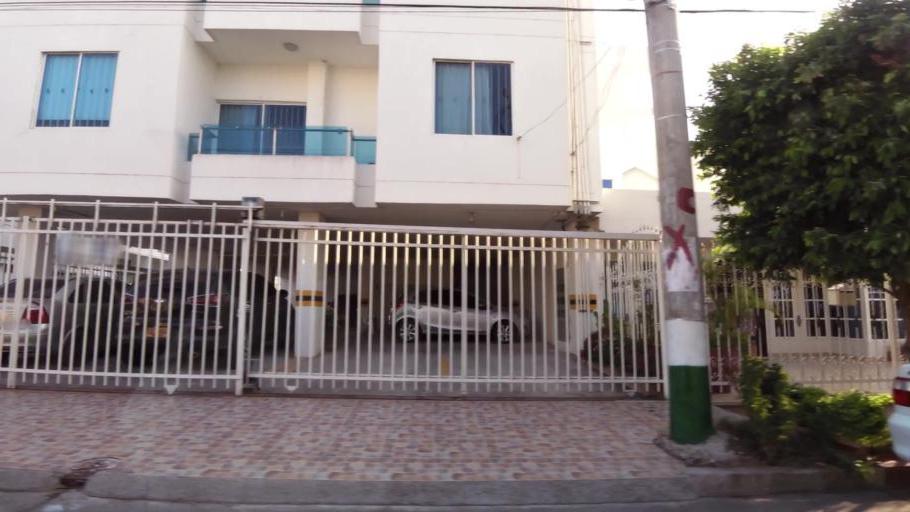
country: CO
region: Bolivar
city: Cartagena
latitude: 10.3923
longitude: -75.5174
